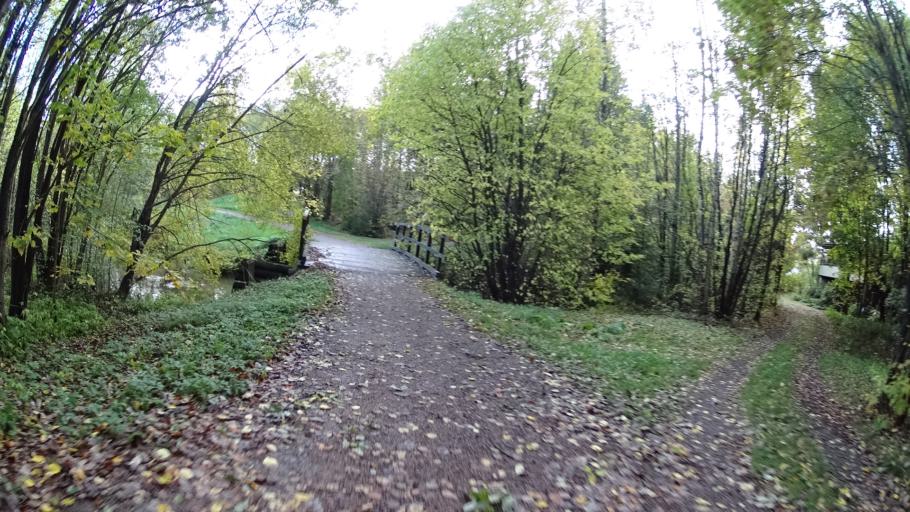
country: FI
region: Uusimaa
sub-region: Helsinki
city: Kilo
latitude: 60.2745
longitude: 24.8161
